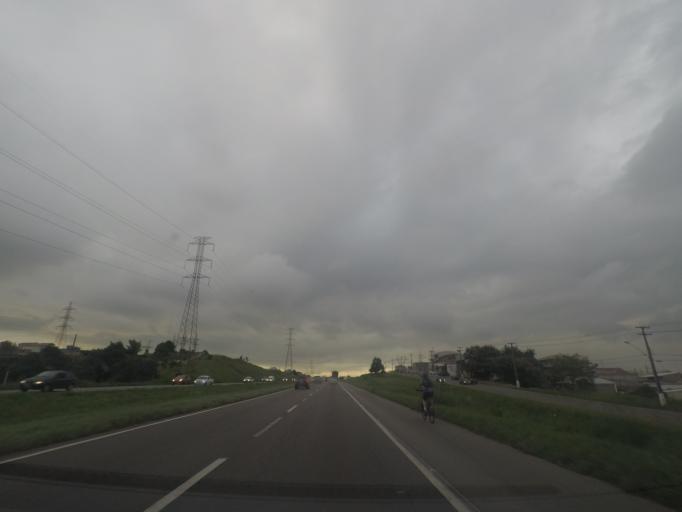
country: BR
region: Parana
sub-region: Curitiba
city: Curitiba
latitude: -25.5025
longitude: -49.3415
